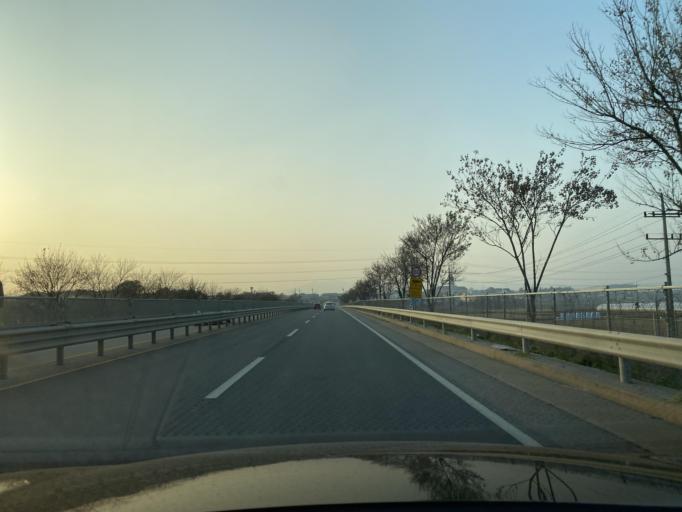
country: KR
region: Chungcheongnam-do
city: Yesan
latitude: 36.6870
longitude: 126.7641
